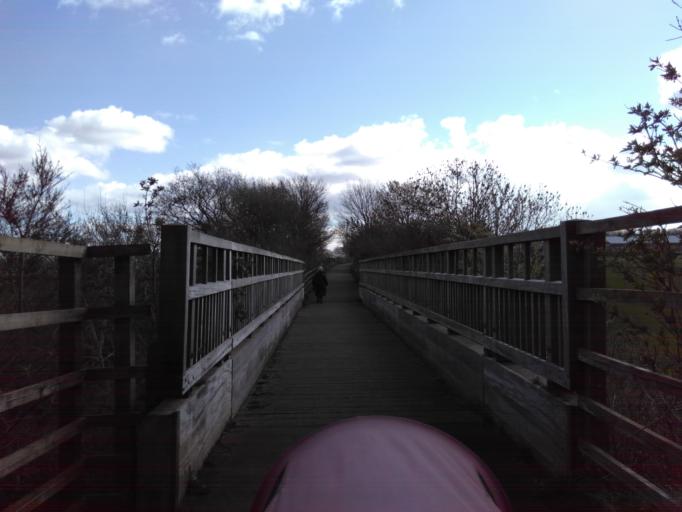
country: GB
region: Scotland
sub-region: Midlothian
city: Loanhead
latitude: 55.8662
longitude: -3.1519
